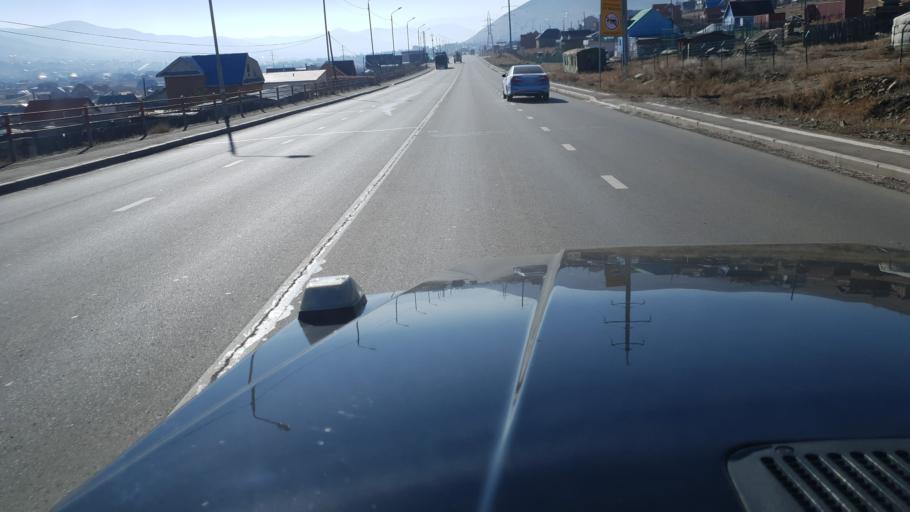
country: MN
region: Ulaanbaatar
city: Ulaanbaatar
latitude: 48.0276
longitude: 106.9121
